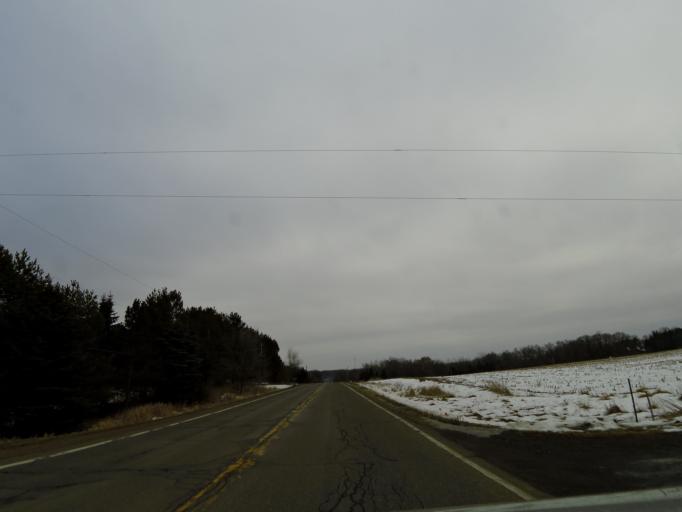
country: US
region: Minnesota
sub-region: Washington County
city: Afton
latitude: 44.8445
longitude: -92.7977
